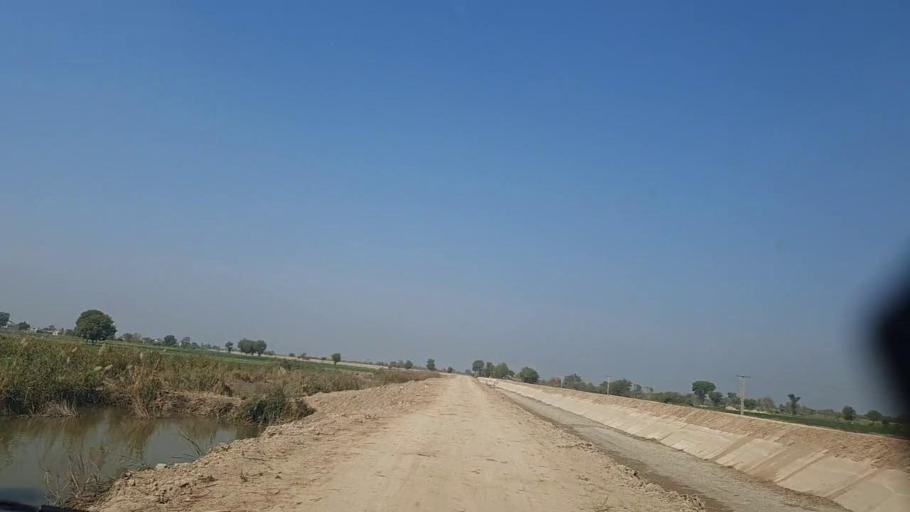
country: PK
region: Sindh
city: Sakrand
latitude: 26.1602
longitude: 68.3267
